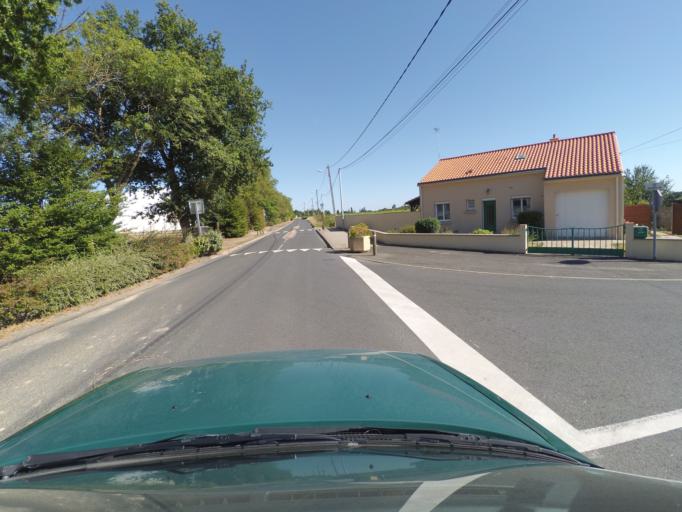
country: FR
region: Pays de la Loire
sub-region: Departement de la Loire-Atlantique
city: Maisdon-sur-Sevre
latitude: 47.0960
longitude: -1.3816
